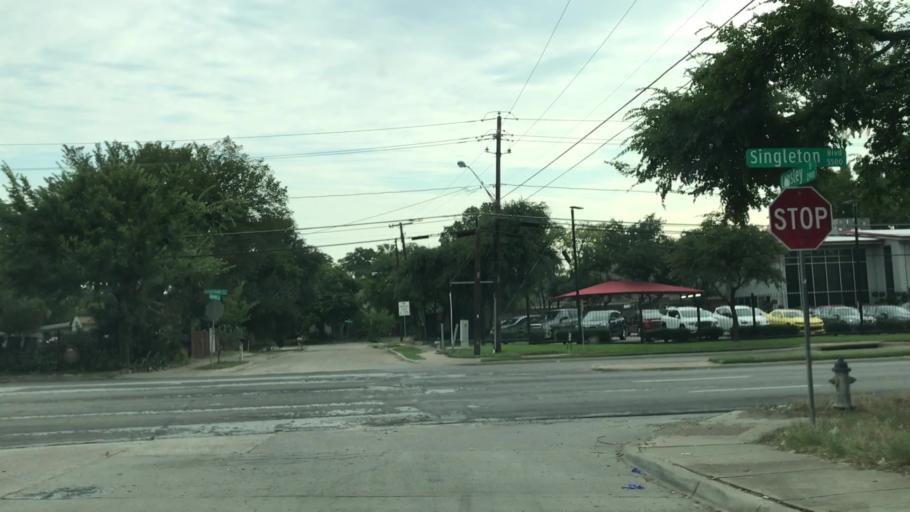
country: US
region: Texas
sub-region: Dallas County
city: Cockrell Hill
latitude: 32.7784
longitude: -96.9120
